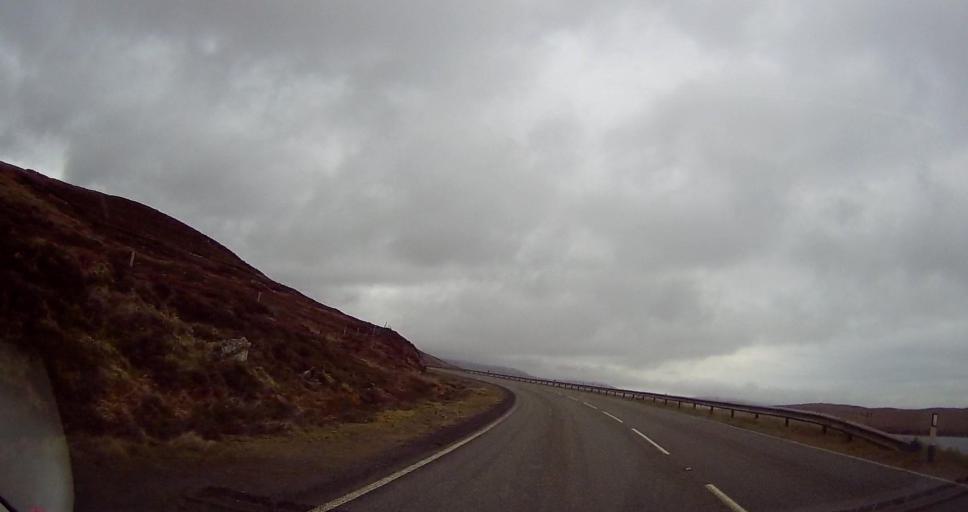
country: GB
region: Scotland
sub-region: Shetland Islands
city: Lerwick
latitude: 60.2496
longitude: -1.2259
